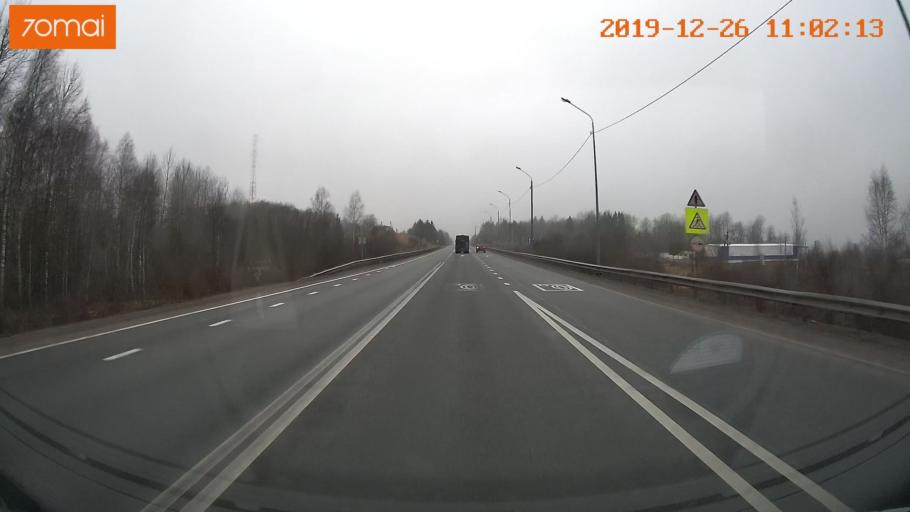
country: RU
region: Vologda
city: Molochnoye
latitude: 59.1587
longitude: 39.4113
